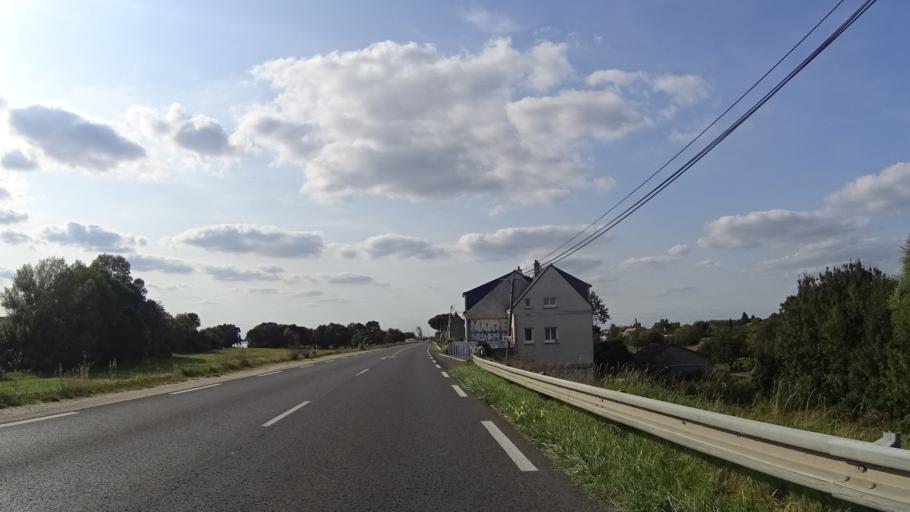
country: FR
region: Pays de la Loire
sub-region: Departement de Maine-et-Loire
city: Saint-Mathurin-sur-Loire
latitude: 47.4127
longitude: -0.3399
